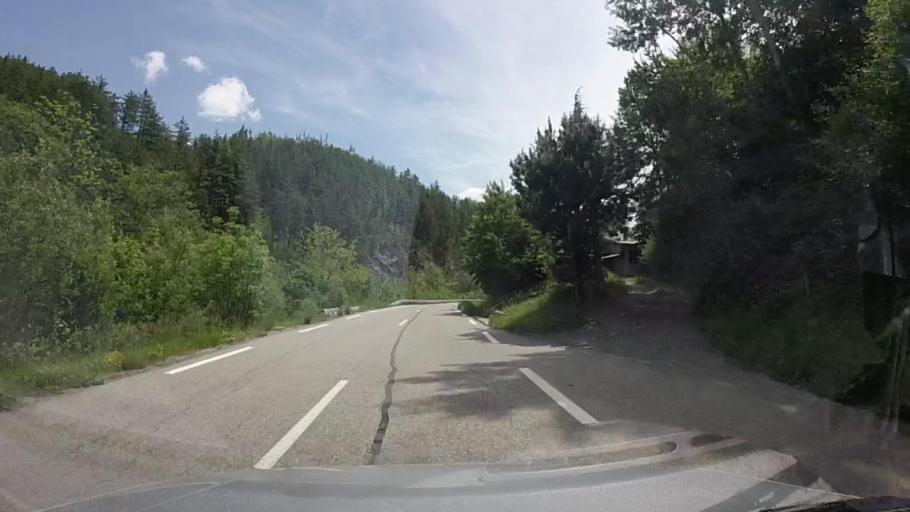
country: FR
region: Provence-Alpes-Cote d'Azur
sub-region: Departement des Alpes-de-Haute-Provence
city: Le Brusquet
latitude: 44.2336
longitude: 6.3594
